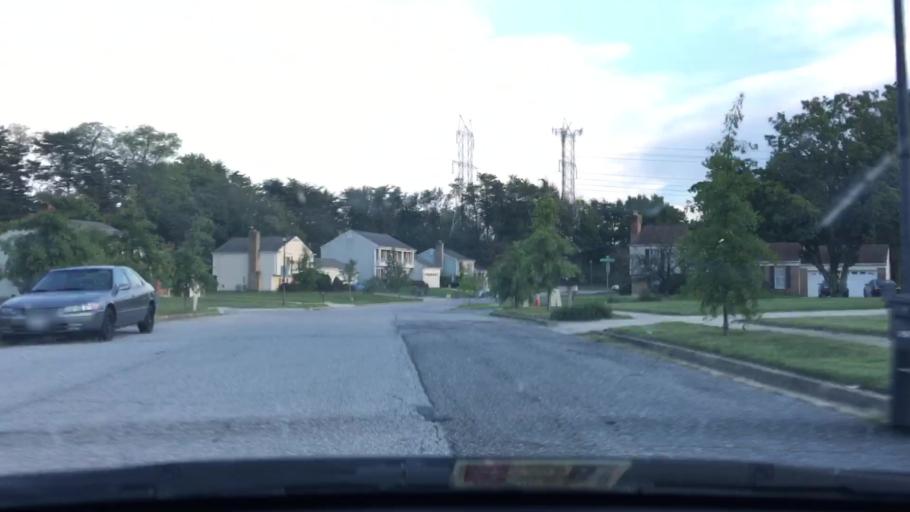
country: US
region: Maryland
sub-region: Prince George's County
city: South Laurel
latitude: 39.0512
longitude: -76.8291
